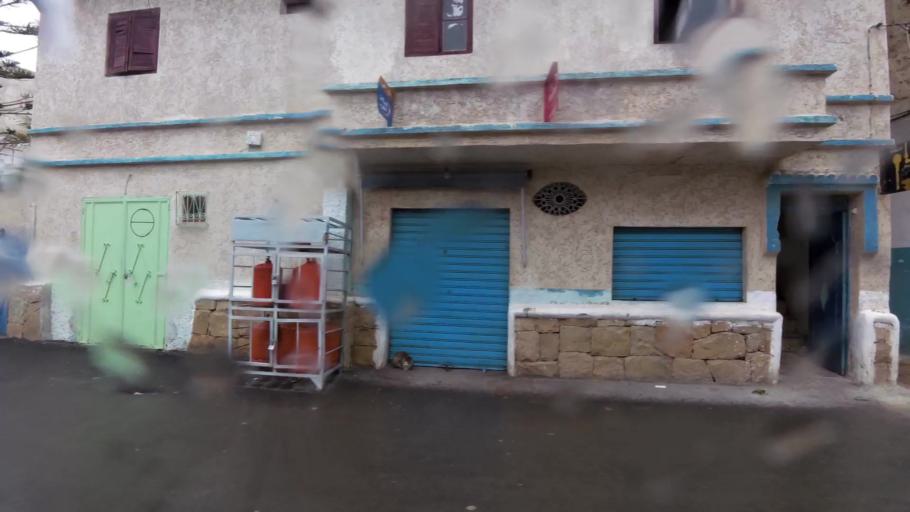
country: MA
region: Tanger-Tetouan
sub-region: Tetouan
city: Martil
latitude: 35.6203
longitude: -5.2804
